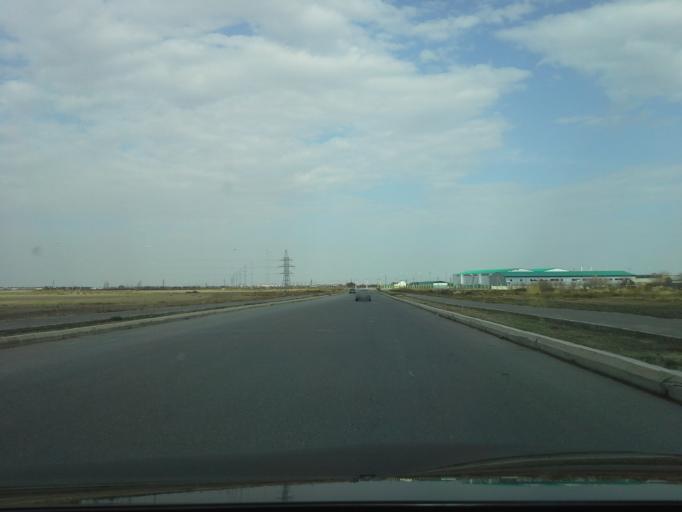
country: TM
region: Ahal
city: Abadan
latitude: 37.9887
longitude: 58.2745
